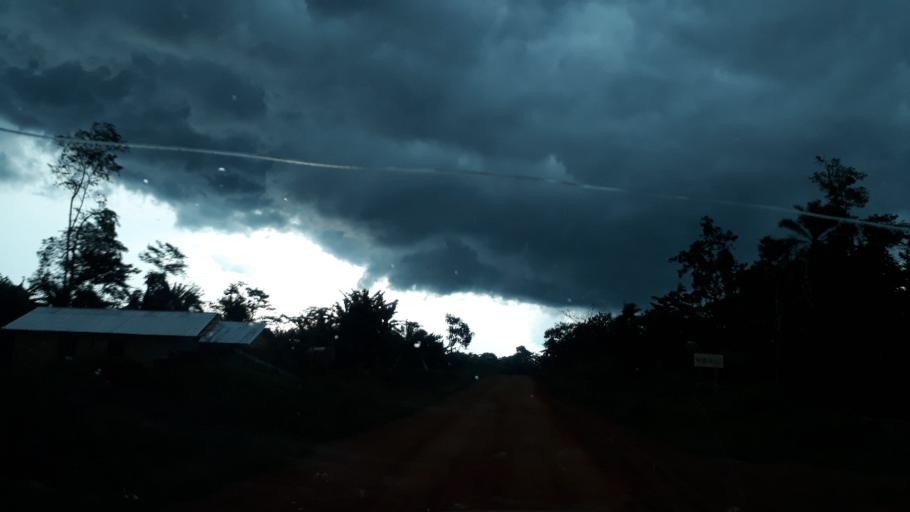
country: CD
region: Nord Kivu
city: Beni
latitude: 1.3481
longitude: 29.2041
